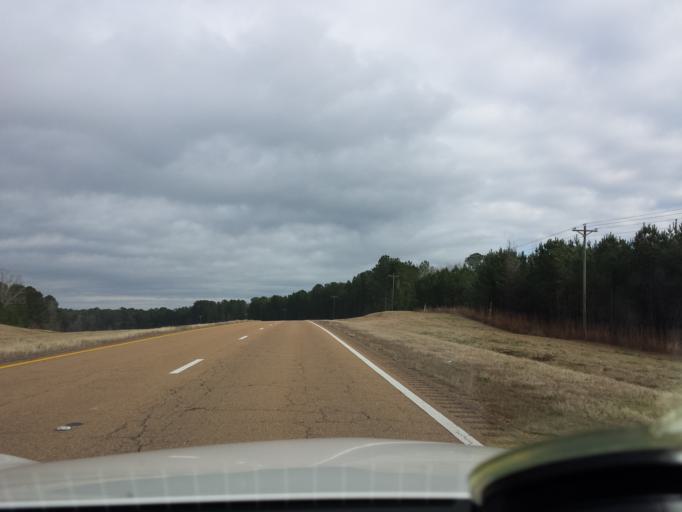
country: US
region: Mississippi
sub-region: Winston County
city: Louisville
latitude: 33.2425
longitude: -88.9712
